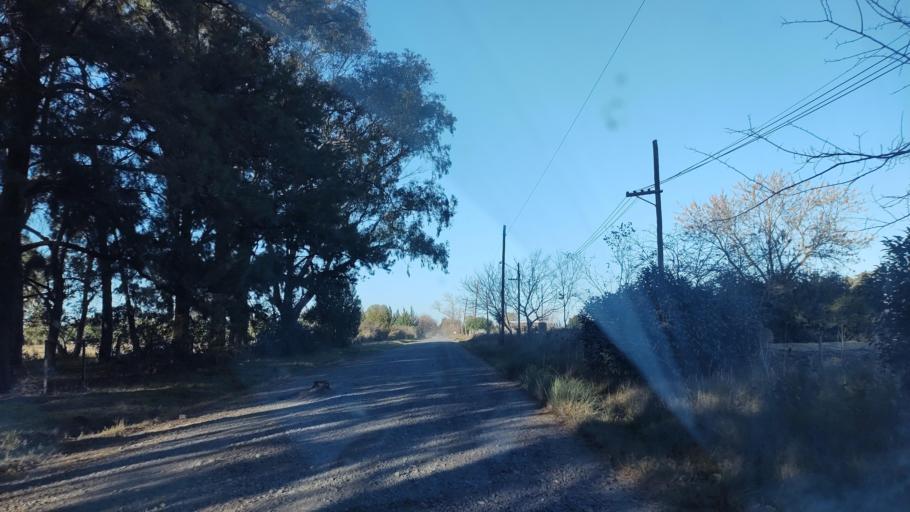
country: AR
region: Buenos Aires
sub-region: Partido de La Plata
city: La Plata
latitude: -34.9083
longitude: -58.0534
